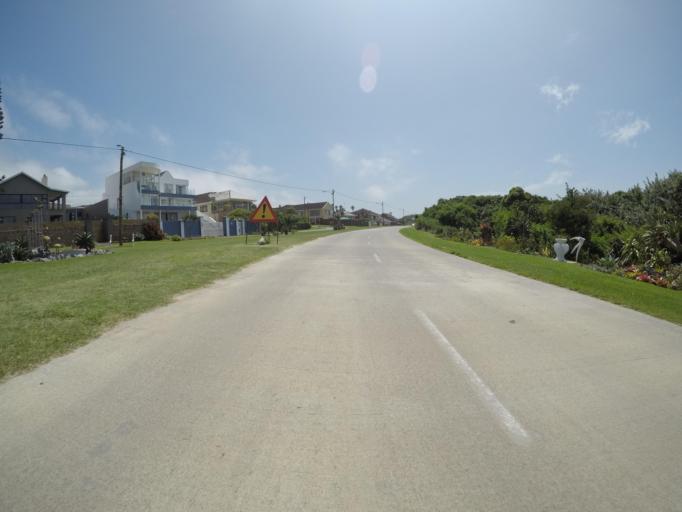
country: ZA
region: Eastern Cape
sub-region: Buffalo City Metropolitan Municipality
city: East London
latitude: -32.9437
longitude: 28.0264
